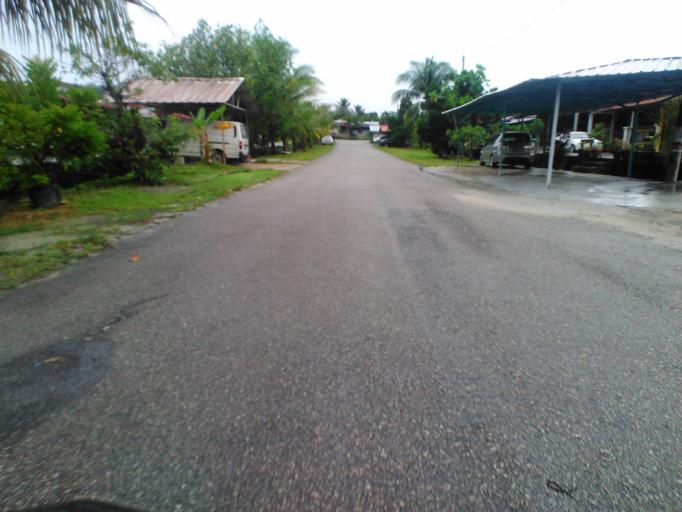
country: MY
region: Kedah
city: Kulim
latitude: 5.3630
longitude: 100.5778
